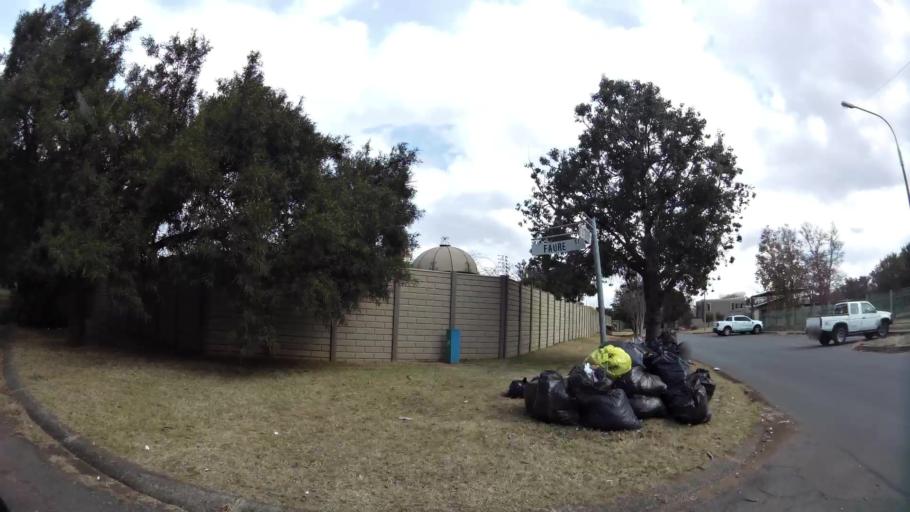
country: ZA
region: Gauteng
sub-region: Sedibeng District Municipality
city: Vanderbijlpark
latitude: -26.7263
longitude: 27.8465
